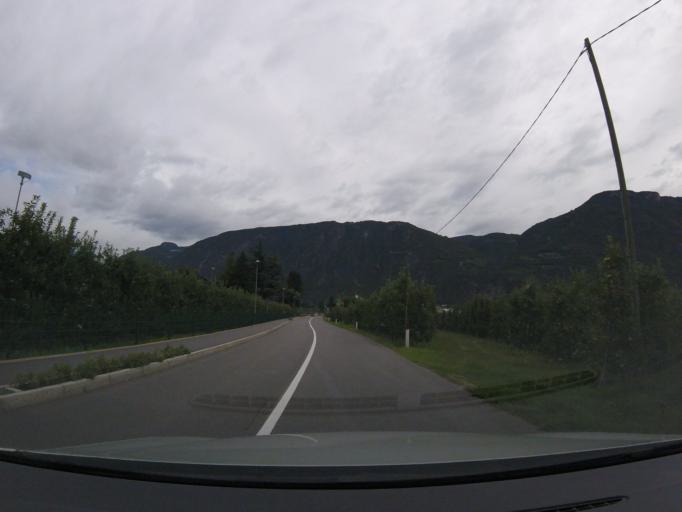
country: IT
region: Trentino-Alto Adige
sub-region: Bolzano
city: Nalles
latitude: 46.5478
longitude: 11.2090
